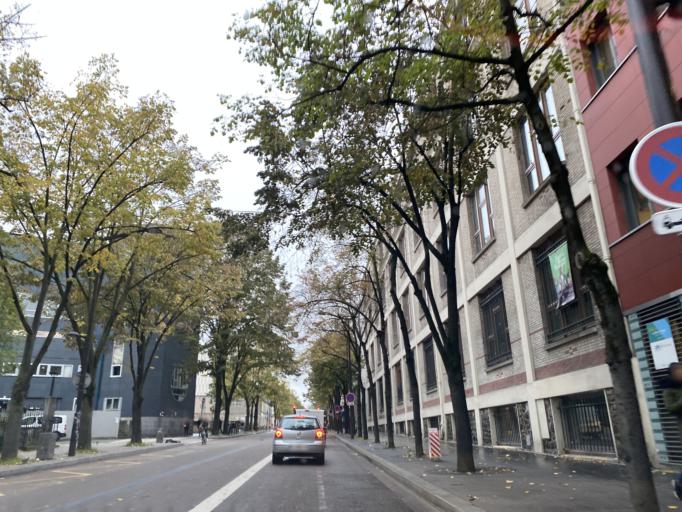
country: FR
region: Ile-de-France
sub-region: Departement de Seine-Saint-Denis
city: Le Pre-Saint-Gervais
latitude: 48.8762
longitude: 2.4061
